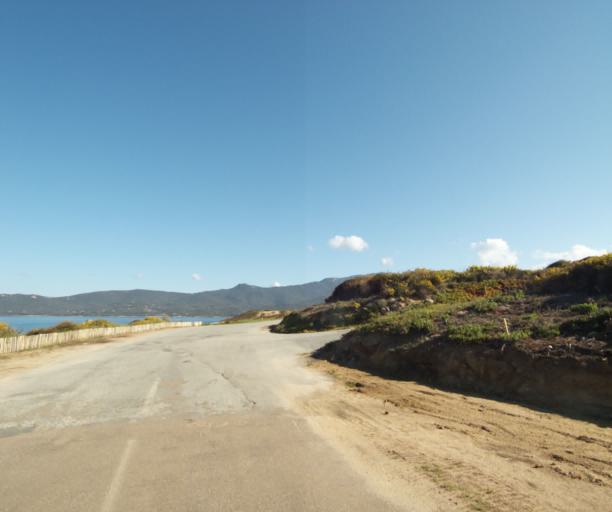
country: FR
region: Corsica
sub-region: Departement de la Corse-du-Sud
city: Propriano
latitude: 41.6657
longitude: 8.8824
